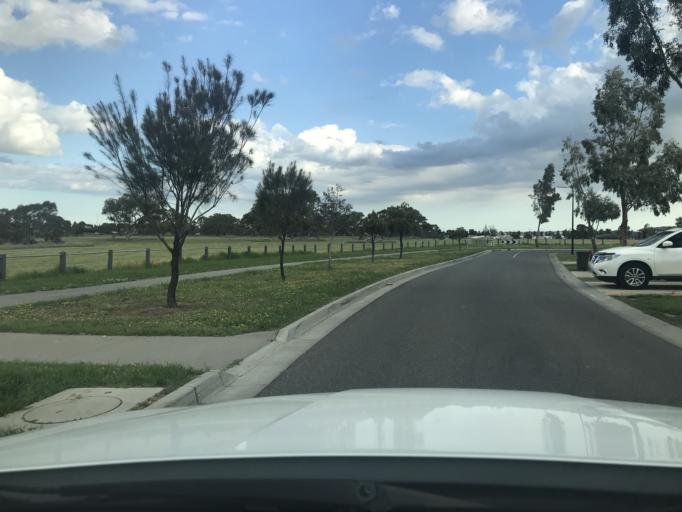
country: AU
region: Victoria
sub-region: Hume
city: Craigieburn
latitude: -37.5763
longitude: 144.9146
